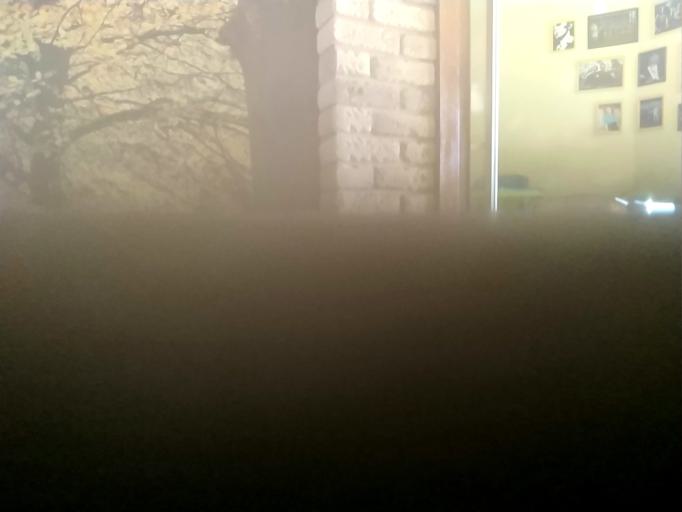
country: RU
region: Kaluga
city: Yukhnov
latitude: 54.7994
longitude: 35.0139
